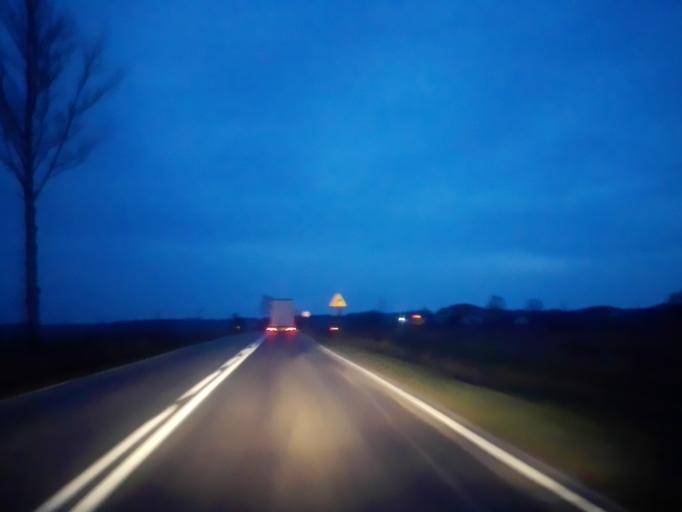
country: PL
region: Podlasie
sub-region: Powiat lomzynski
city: Sniadowo
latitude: 53.0754
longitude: 22.0163
